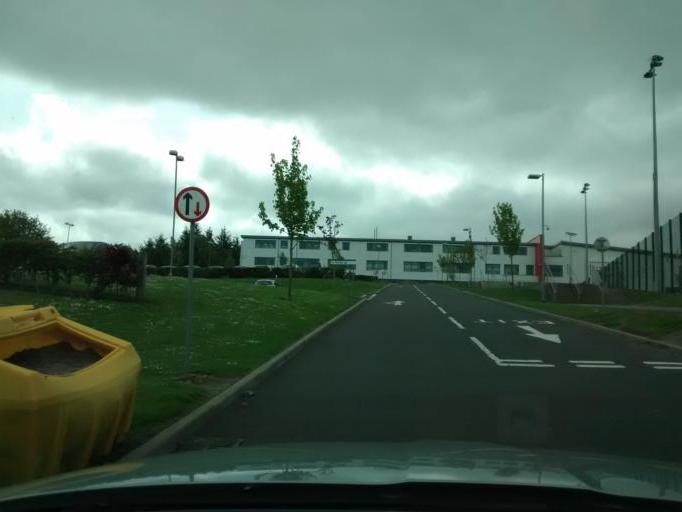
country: GB
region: Scotland
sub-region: West Lothian
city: Armadale
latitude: 55.8964
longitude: -3.7150
